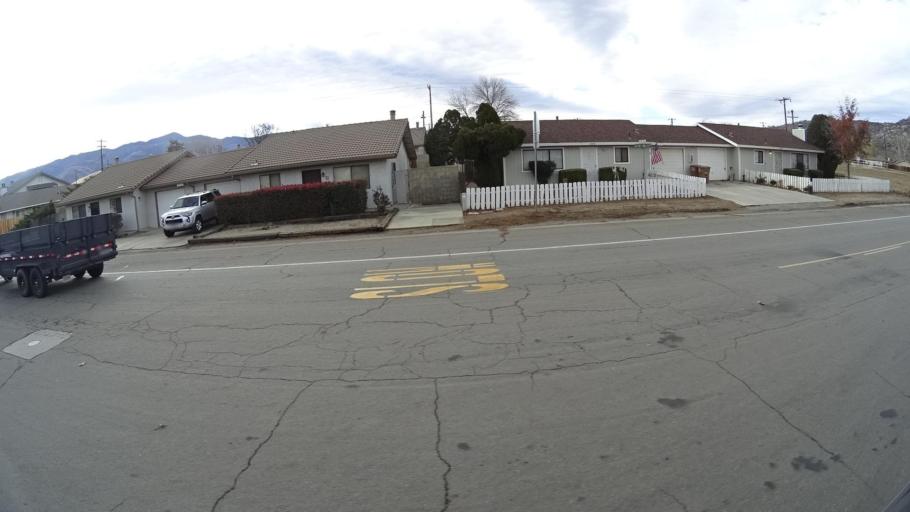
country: US
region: California
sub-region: Kern County
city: Golden Hills
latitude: 35.1326
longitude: -118.4903
